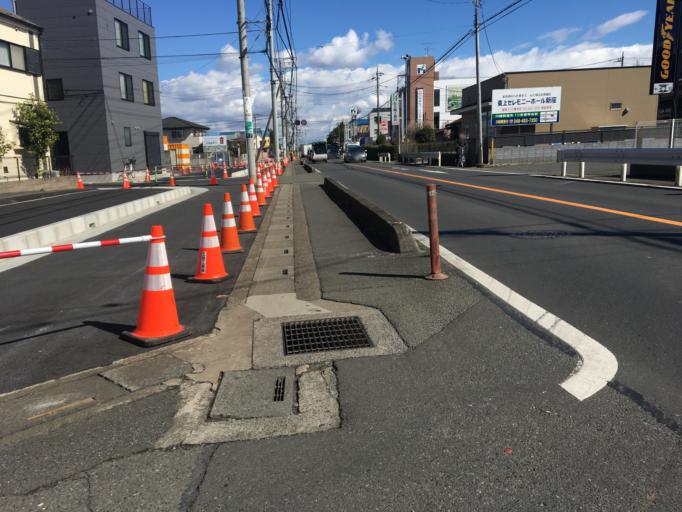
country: JP
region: Saitama
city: Shiki
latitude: 35.7948
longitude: 139.5534
